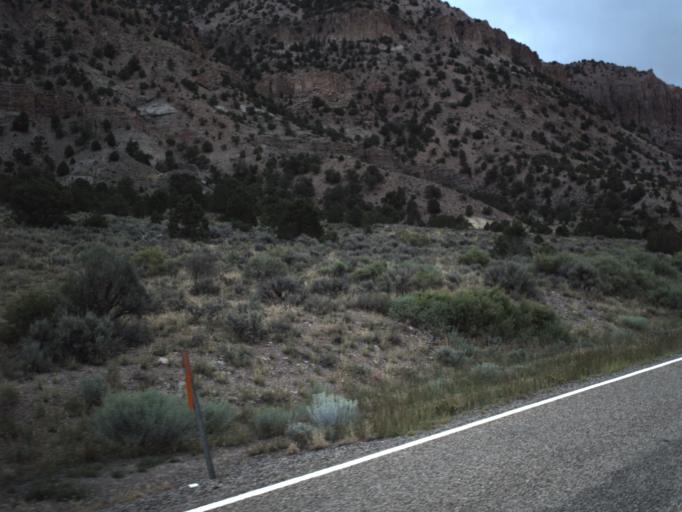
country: US
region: Utah
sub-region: Piute County
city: Junction
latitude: 38.1959
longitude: -112.1187
